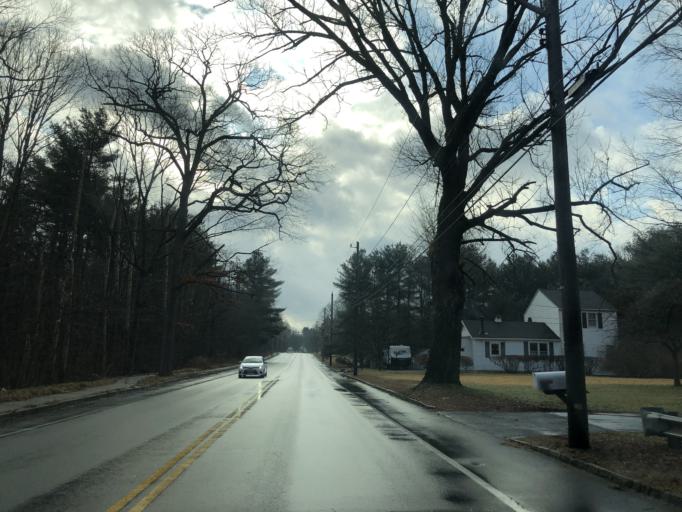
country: US
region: Massachusetts
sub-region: Bristol County
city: Attleboro
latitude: 41.9779
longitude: -71.2926
